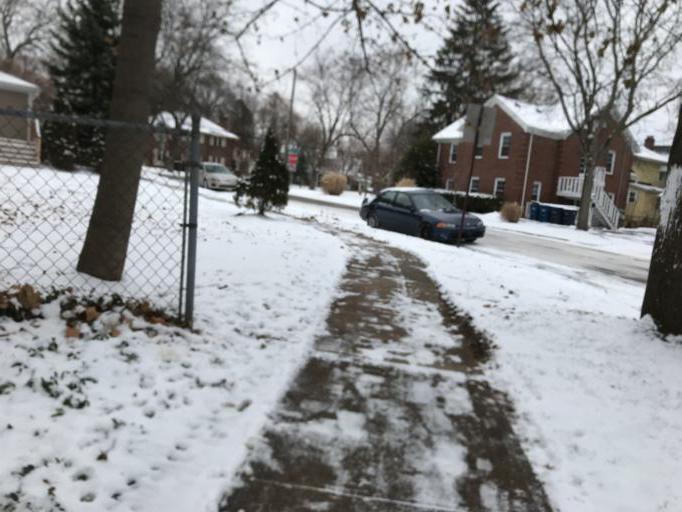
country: US
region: Michigan
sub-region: Washtenaw County
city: Ann Arbor
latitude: 42.2618
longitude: -83.7315
